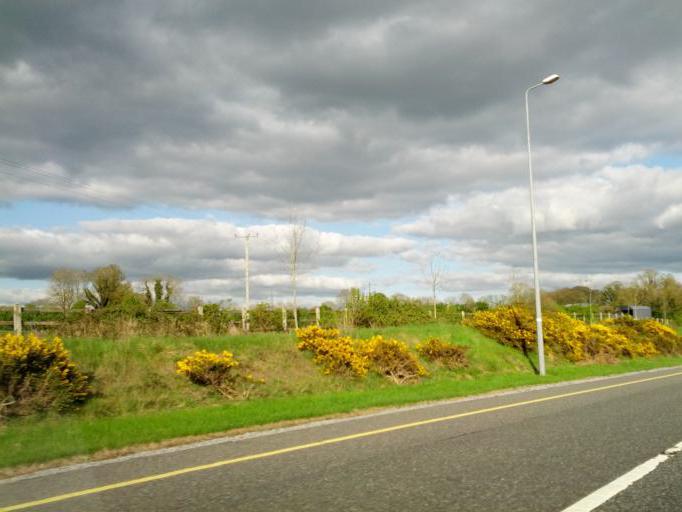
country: IE
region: Leinster
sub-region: An Iarmhi
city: Moate
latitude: 53.3922
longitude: -7.7756
